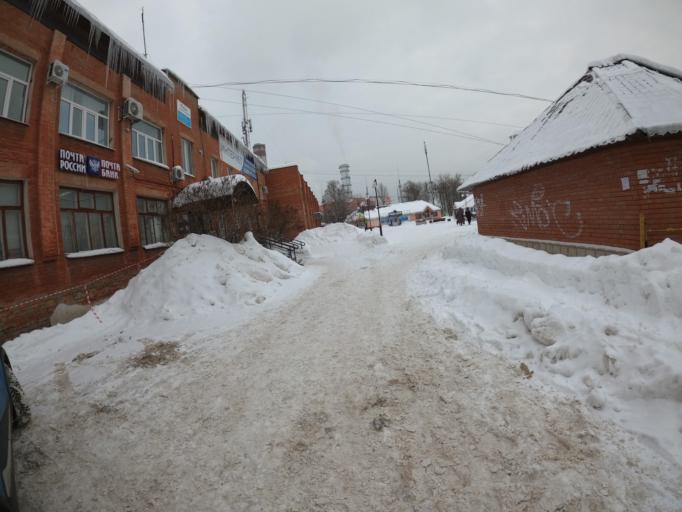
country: RU
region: Moskovskaya
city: Elektrogorsk
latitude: 55.8838
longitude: 38.7826
